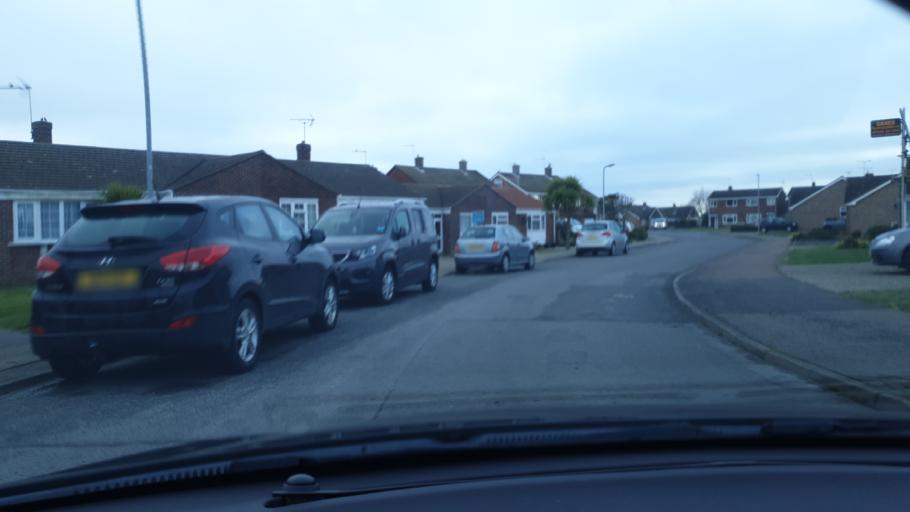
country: GB
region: England
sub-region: Essex
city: Walton-on-the-Naze
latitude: 51.8478
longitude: 1.2512
